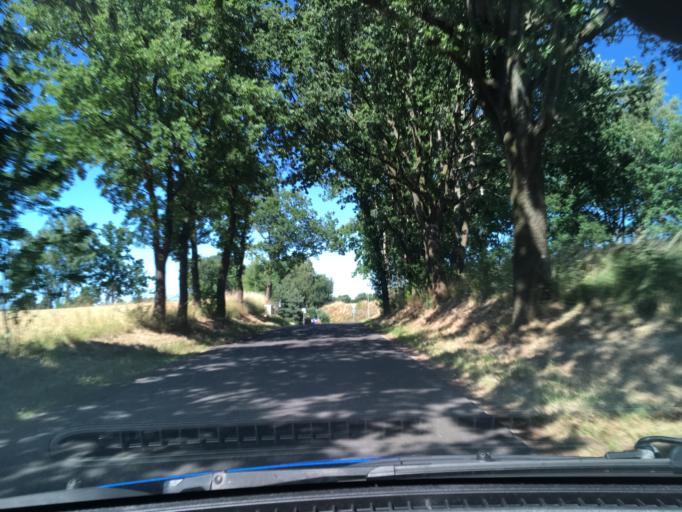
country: DE
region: Lower Saxony
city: Seevetal
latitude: 53.3767
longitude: 9.9662
